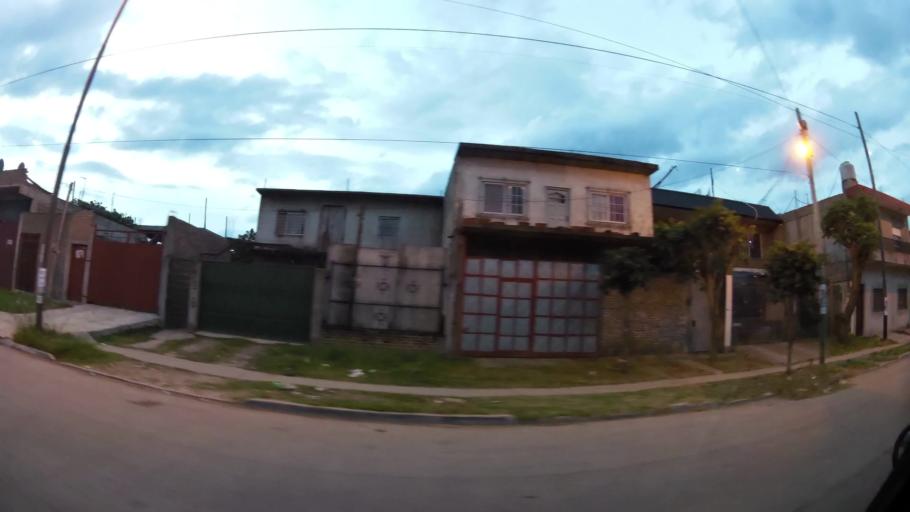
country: AR
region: Buenos Aires
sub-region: Partido de Quilmes
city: Quilmes
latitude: -34.7202
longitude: -58.2360
